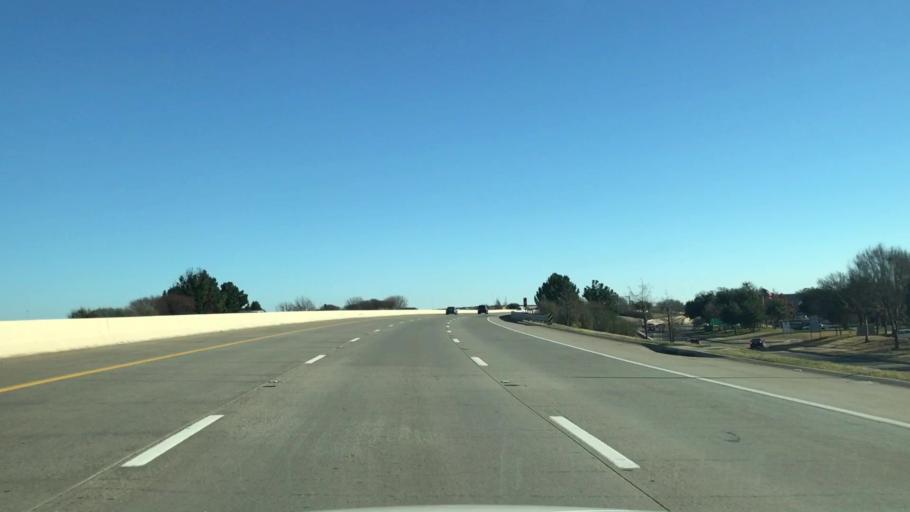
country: US
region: Texas
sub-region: Dallas County
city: Coppell
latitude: 32.9913
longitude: -96.9777
